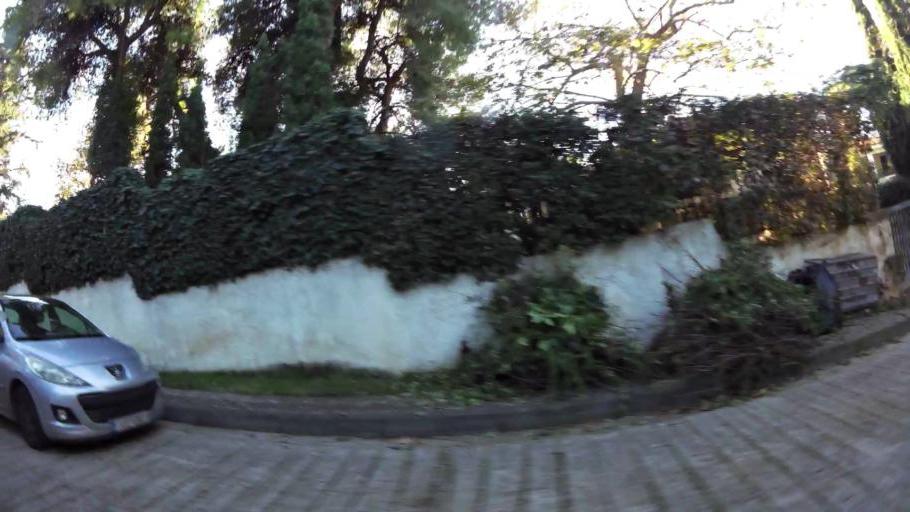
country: GR
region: Attica
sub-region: Nomarchia Athinas
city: Ekali
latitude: 38.1108
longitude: 23.8508
